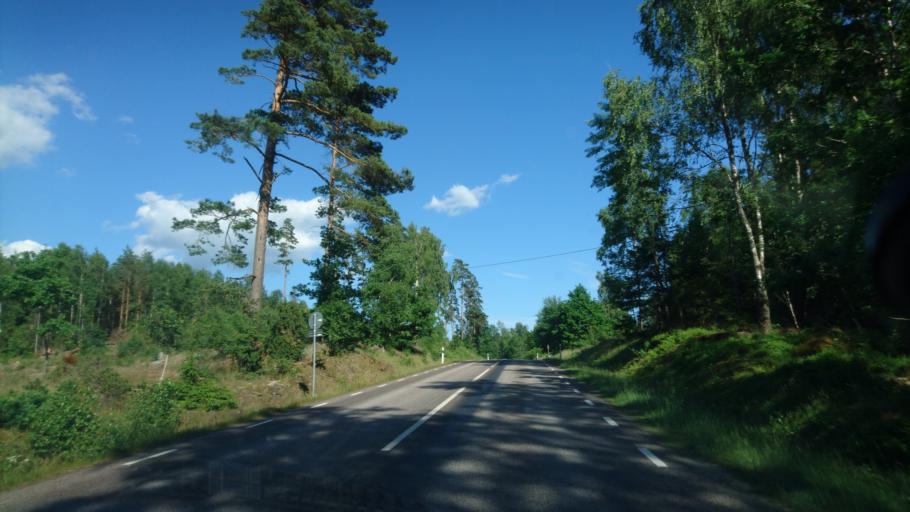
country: SE
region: Skane
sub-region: Osby Kommun
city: Lonsboda
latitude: 56.3917
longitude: 14.3384
